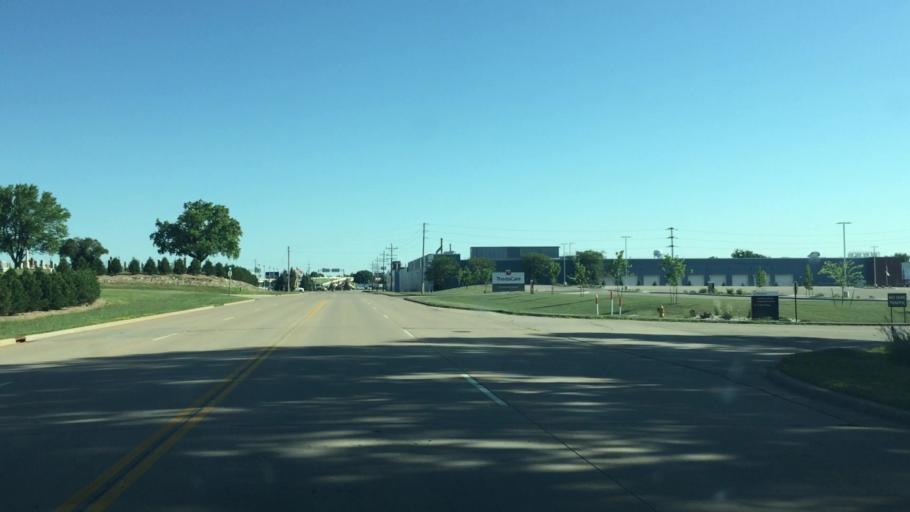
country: US
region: Wisconsin
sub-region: Winnebago County
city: Neenah
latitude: 44.1943
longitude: -88.4851
